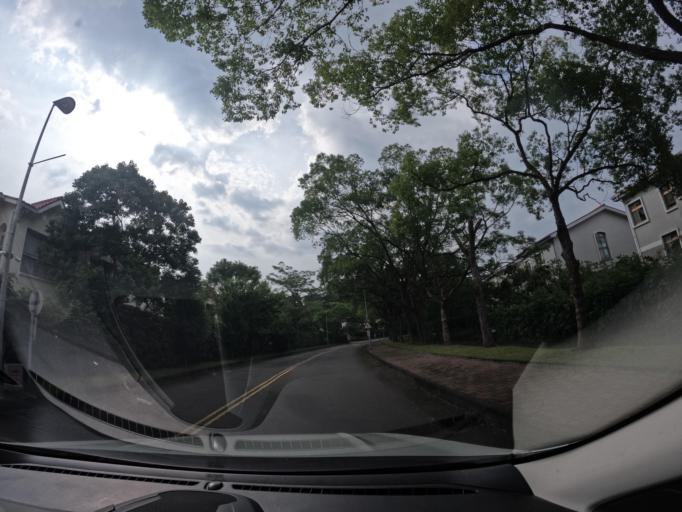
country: TW
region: Taiwan
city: Daxi
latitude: 24.8873
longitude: 121.3223
